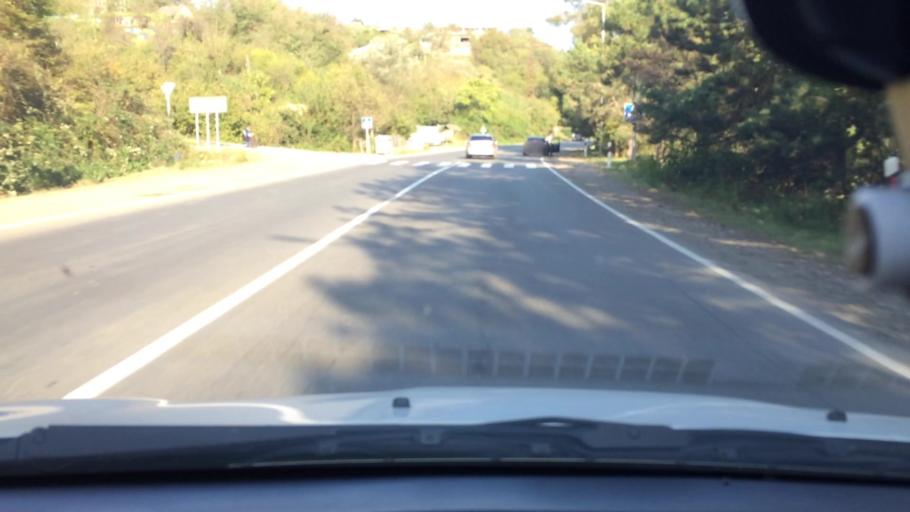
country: GE
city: Shorapani
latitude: 42.0930
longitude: 43.0787
